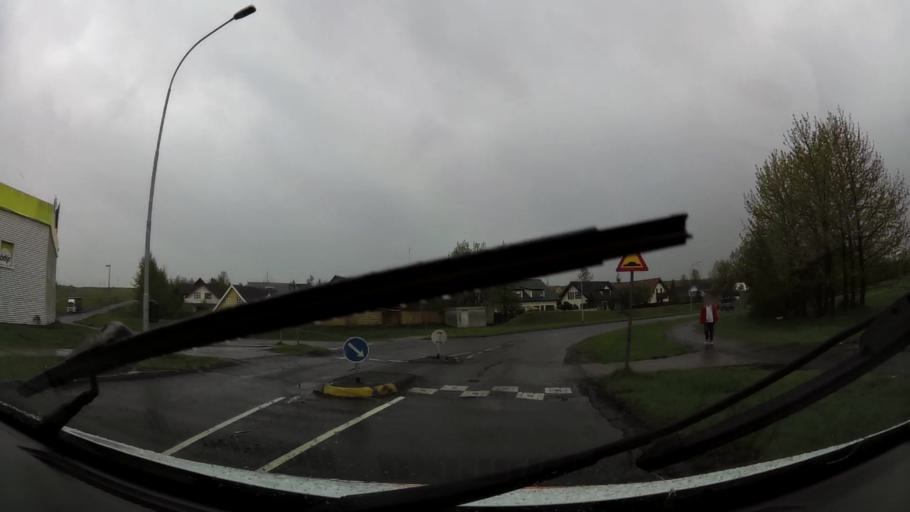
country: IS
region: Capital Region
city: Reykjavik
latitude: 64.0972
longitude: -21.8272
